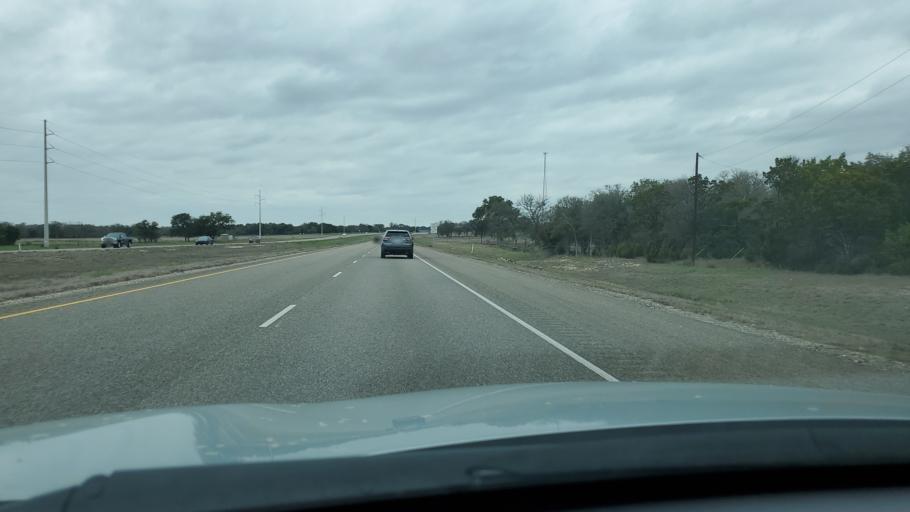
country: US
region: Texas
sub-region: Williamson County
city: Florence
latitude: 30.7667
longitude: -97.7512
